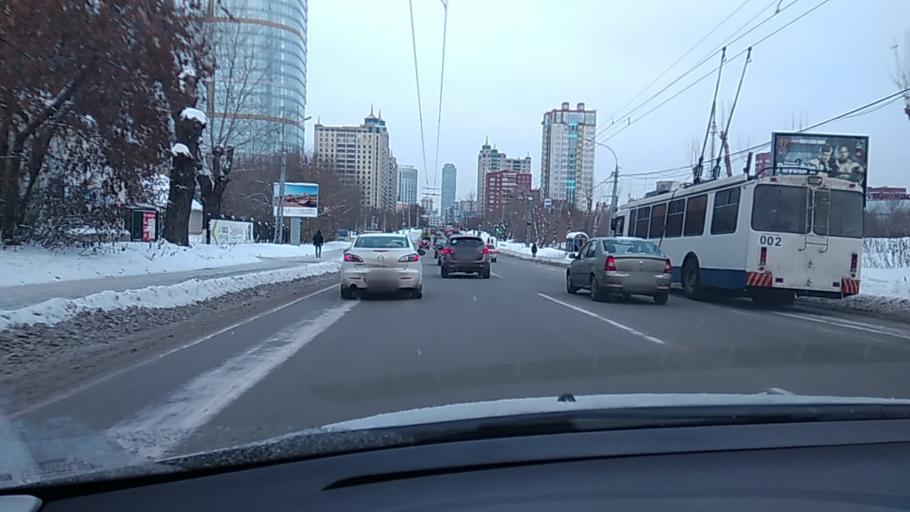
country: RU
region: Sverdlovsk
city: Yekaterinburg
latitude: 56.8180
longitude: 60.6202
